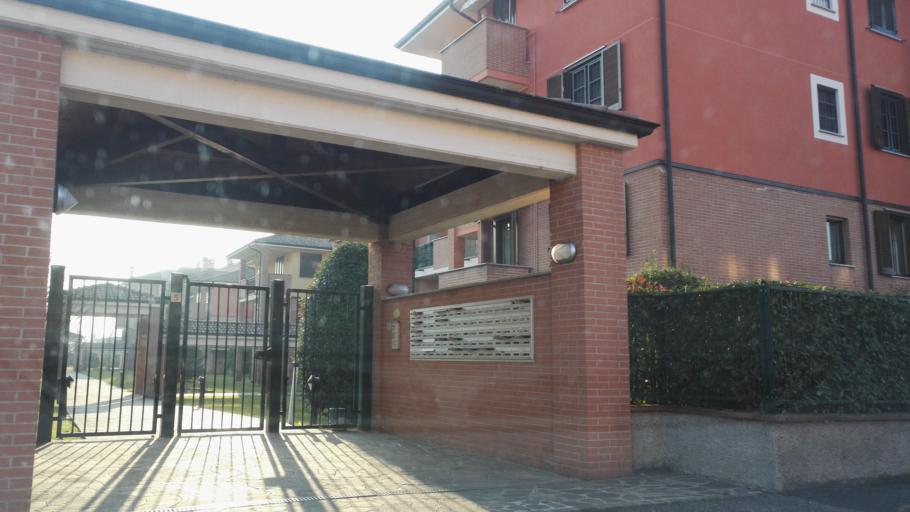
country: IT
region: Lombardy
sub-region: Citta metropolitana di Milano
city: Tribiano
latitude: 45.4170
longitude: 9.3714
